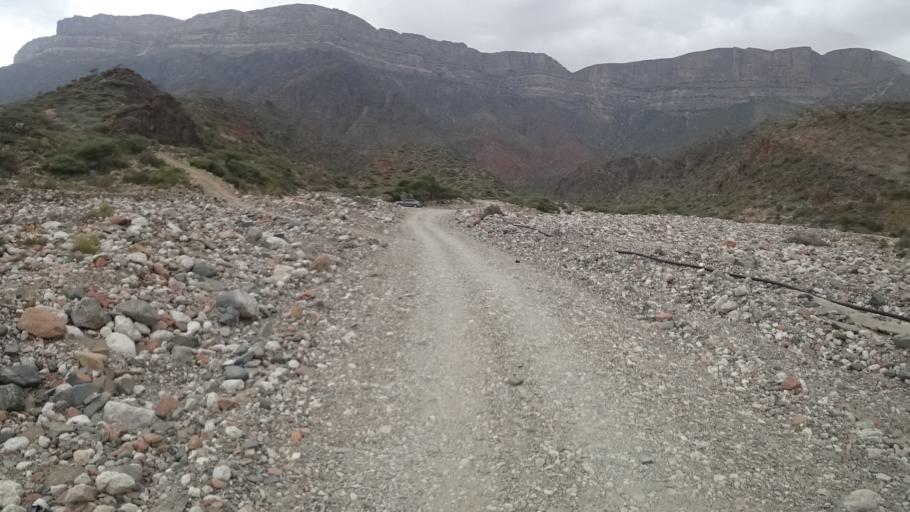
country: OM
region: Zufar
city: Salalah
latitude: 17.1775
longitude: 54.9492
